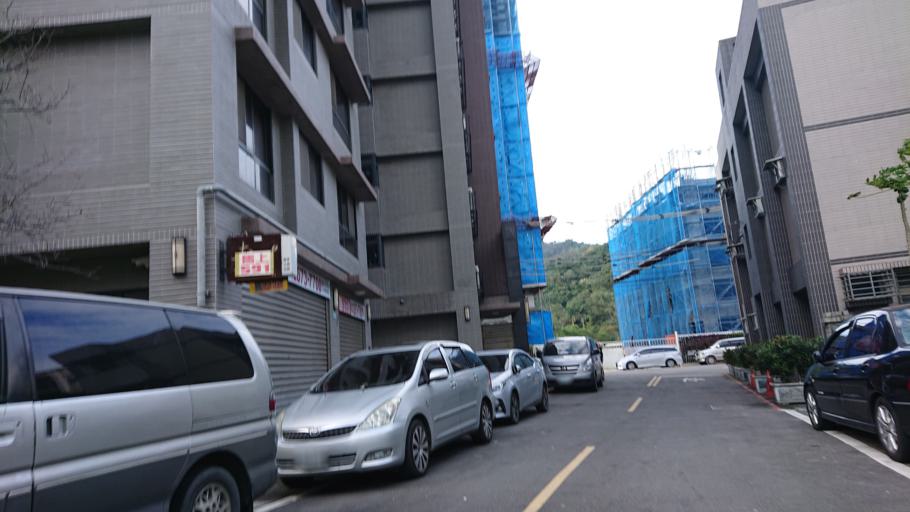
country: TW
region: Taiwan
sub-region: Taoyuan
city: Taoyuan
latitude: 24.9264
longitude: 121.3662
